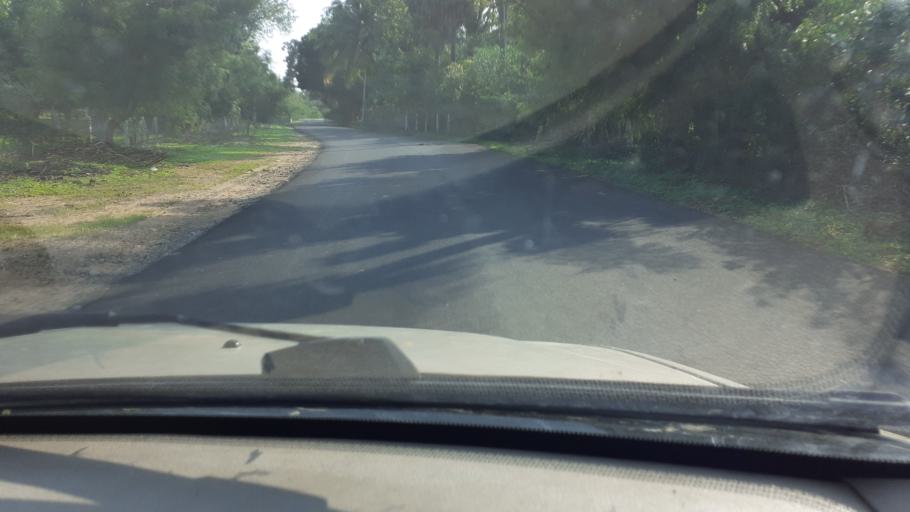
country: IN
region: Tamil Nadu
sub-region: Thoothukkudi
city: Eral
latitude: 8.5756
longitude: 78.0223
